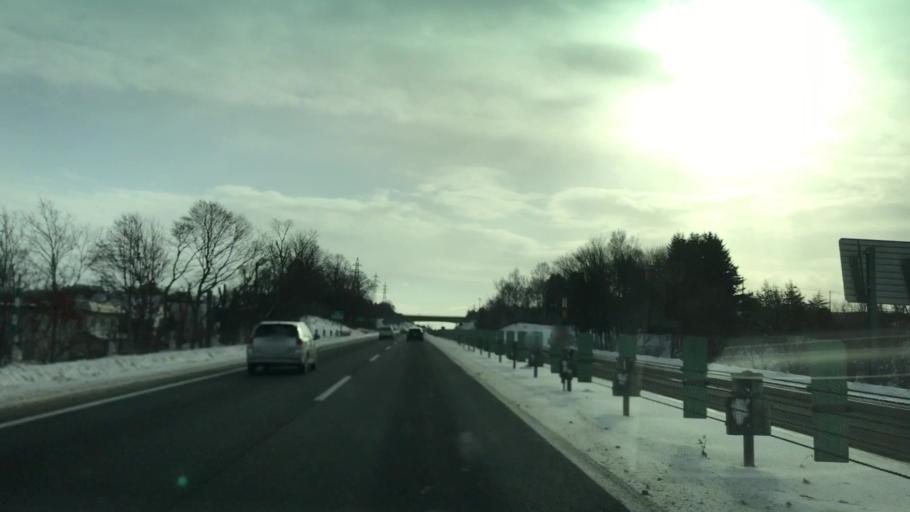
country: JP
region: Hokkaido
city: Kitahiroshima
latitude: 42.9696
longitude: 141.4885
